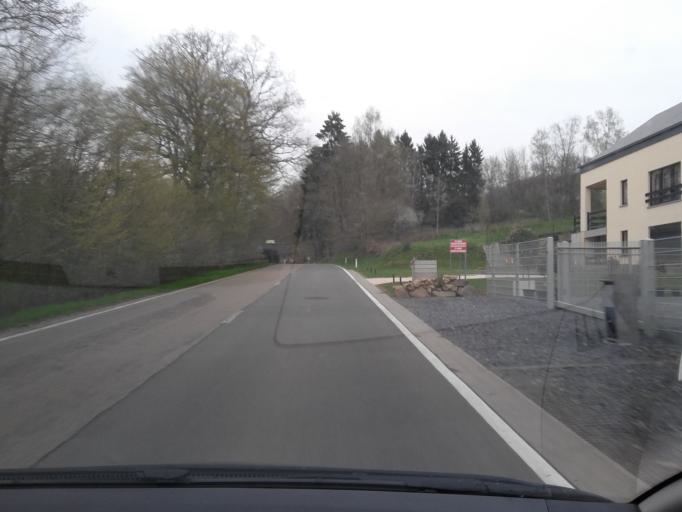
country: BE
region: Wallonia
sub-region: Province du Luxembourg
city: Herbeumont
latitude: 49.7729
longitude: 5.2360
